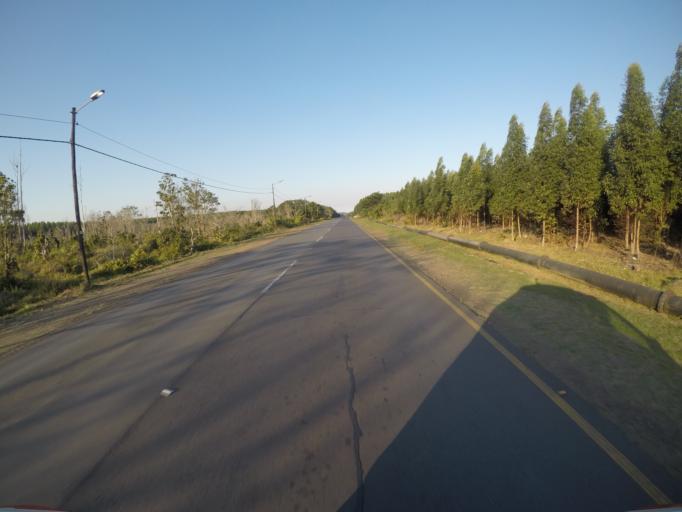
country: ZA
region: KwaZulu-Natal
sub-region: uThungulu District Municipality
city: KwaMbonambi
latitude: -28.6832
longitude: 32.1639
